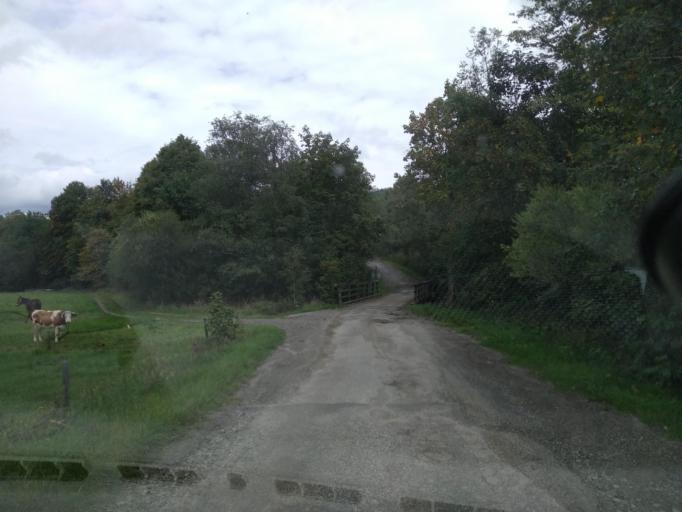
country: PL
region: Lesser Poland Voivodeship
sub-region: Powiat gorlicki
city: Uscie Gorlickie
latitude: 49.5472
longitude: 21.1868
